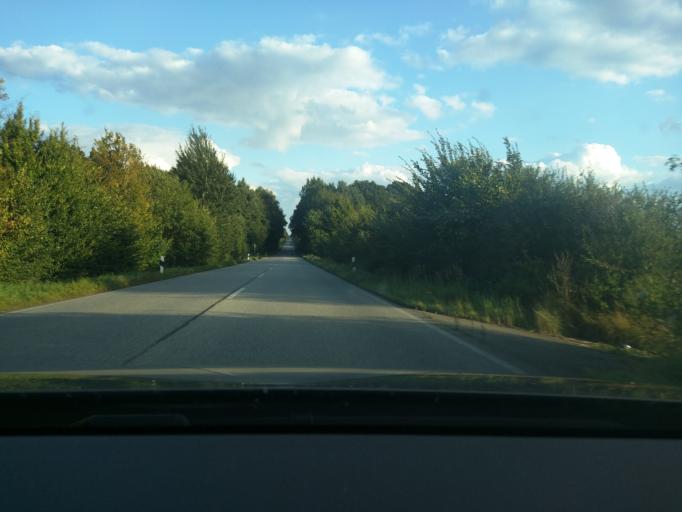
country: DE
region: Schleswig-Holstein
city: Wangelau
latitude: 53.4633
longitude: 10.5437
